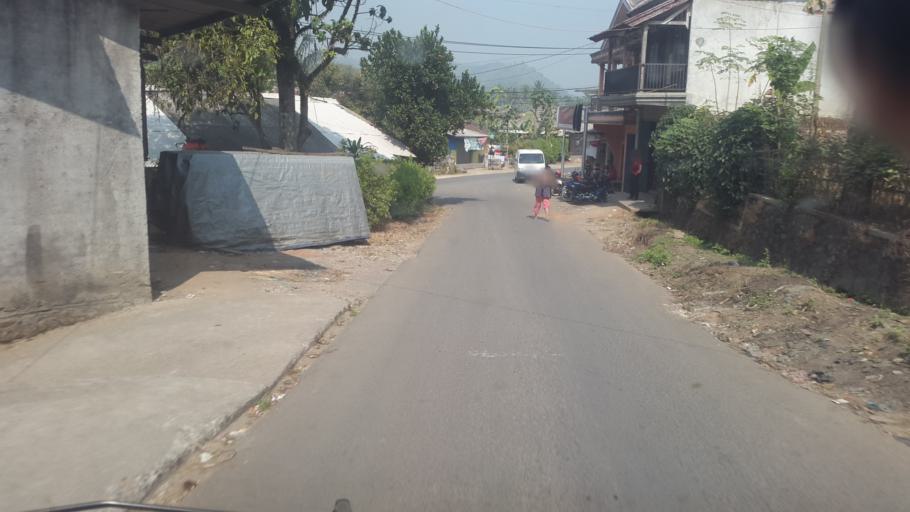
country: ID
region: West Java
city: Pasirreungit
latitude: -6.9431
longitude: 107.0060
